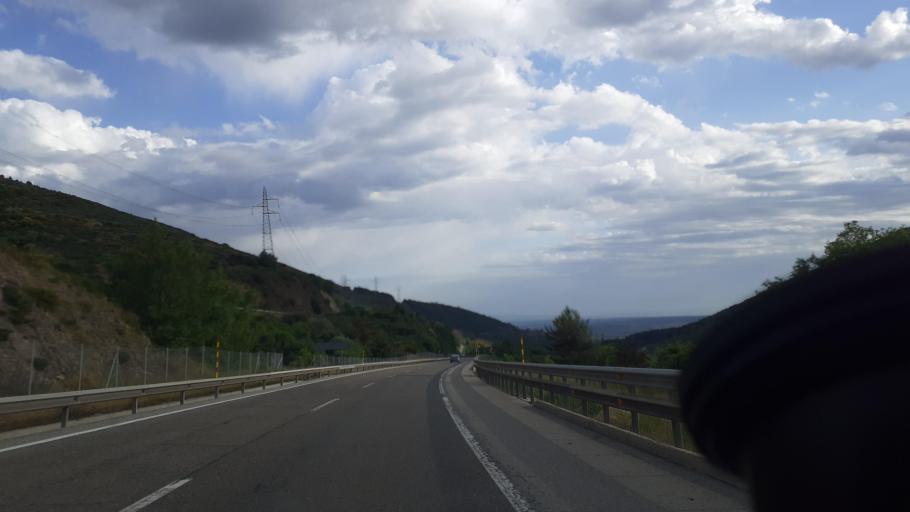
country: ES
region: Madrid
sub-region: Provincia de Madrid
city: Somosierra
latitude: 41.1471
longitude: -3.5832
